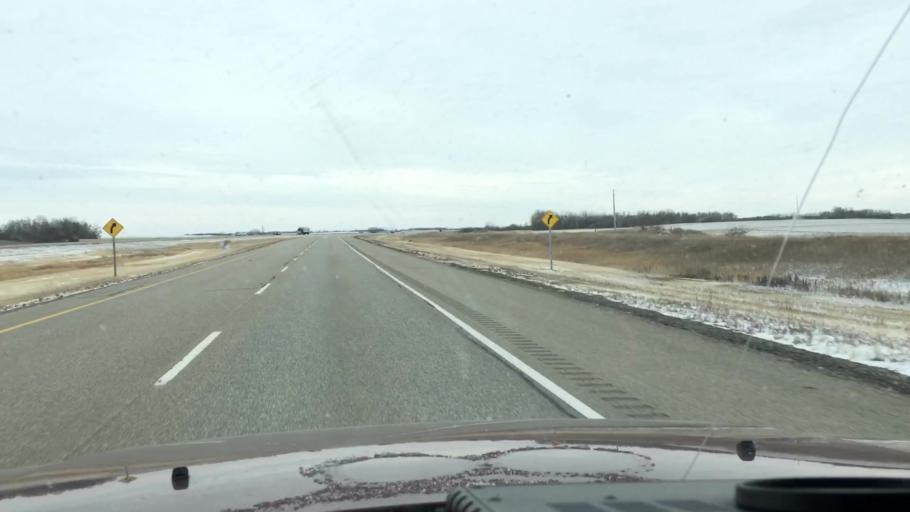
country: CA
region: Saskatchewan
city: Watrous
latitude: 51.3363
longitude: -106.0893
